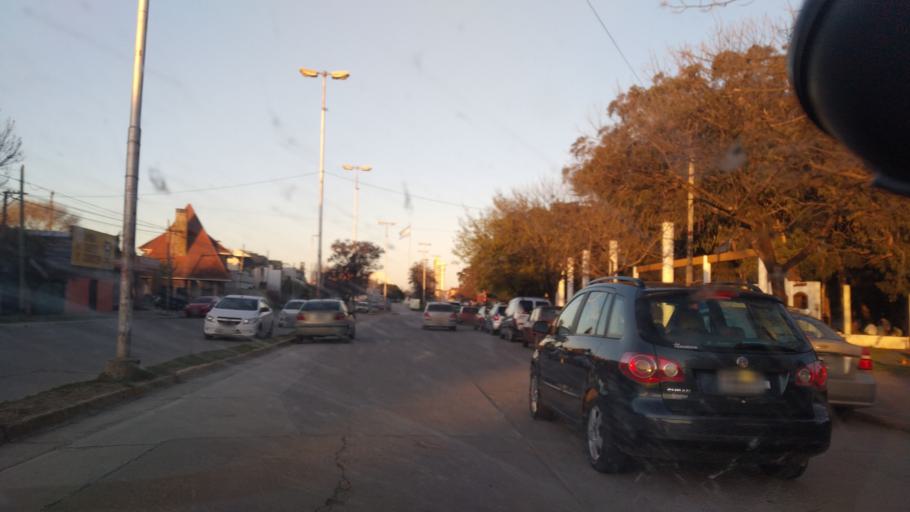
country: AR
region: Buenos Aires
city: Necochea
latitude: -38.5812
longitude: -58.7390
